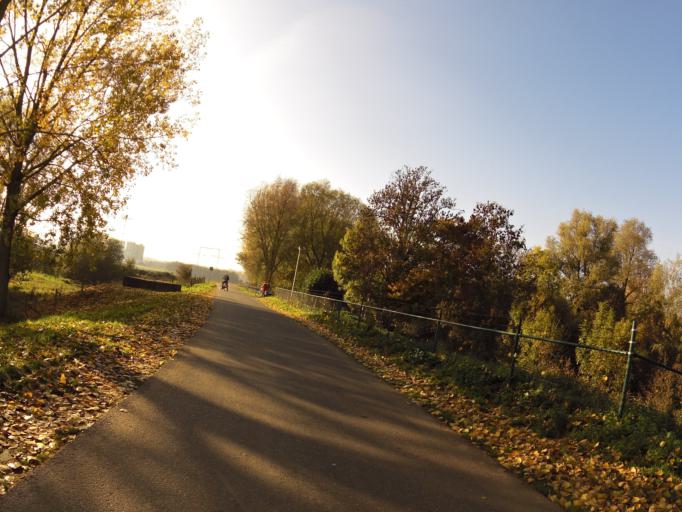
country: NL
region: North Brabant
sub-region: Gemeente 's-Hertogenbosch
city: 's-Hertogenbosch
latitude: 51.7142
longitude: 5.2828
